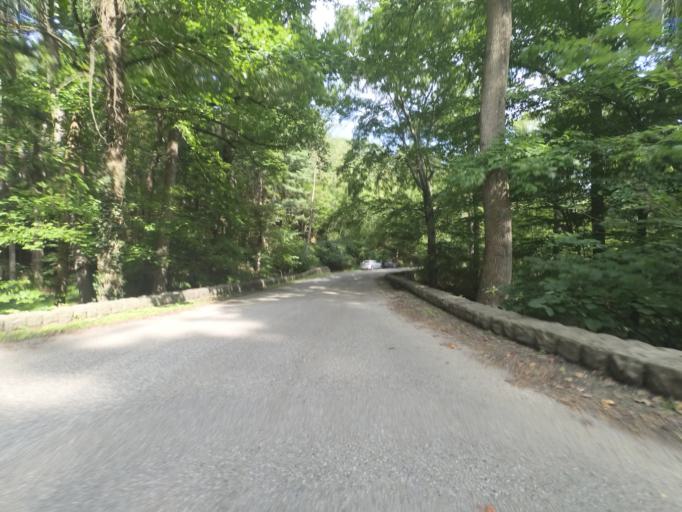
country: US
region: West Virginia
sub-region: Cabell County
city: Huntington
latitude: 38.4187
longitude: -82.3944
